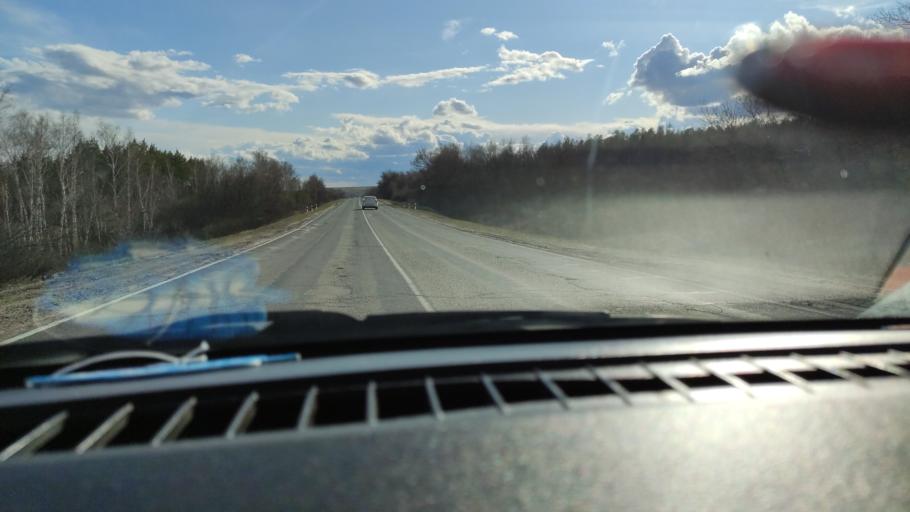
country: RU
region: Saratov
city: Sennoy
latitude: 52.1139
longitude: 46.8346
